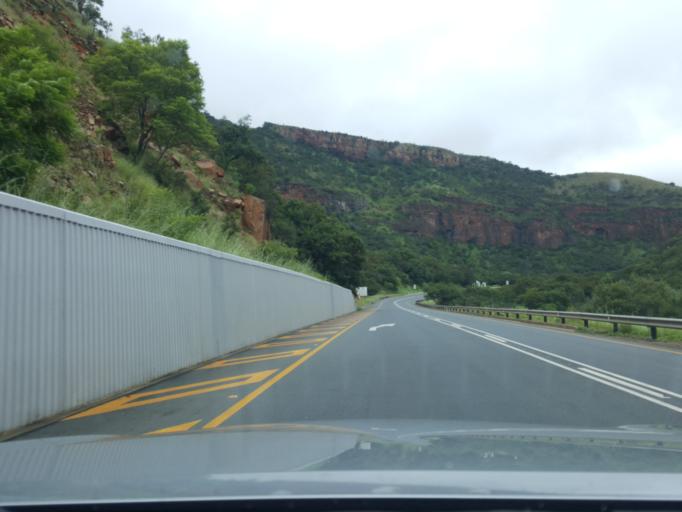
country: ZA
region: Mpumalanga
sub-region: Nkangala District Municipality
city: Belfast
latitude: -25.6458
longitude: 30.3682
